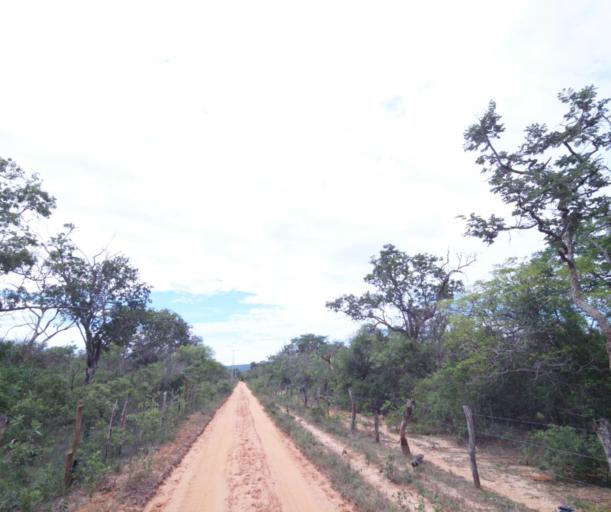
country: BR
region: Bahia
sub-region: Carinhanha
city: Carinhanha
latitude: -14.2391
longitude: -44.3818
